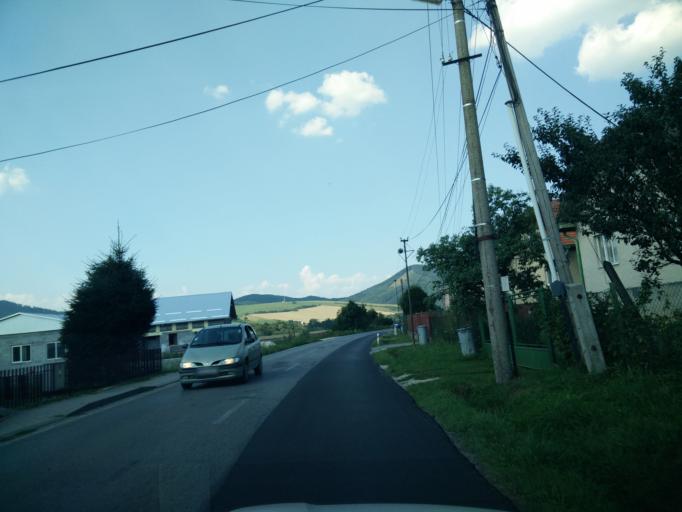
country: SK
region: Zilinsky
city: Rajec
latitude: 49.1092
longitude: 18.6468
